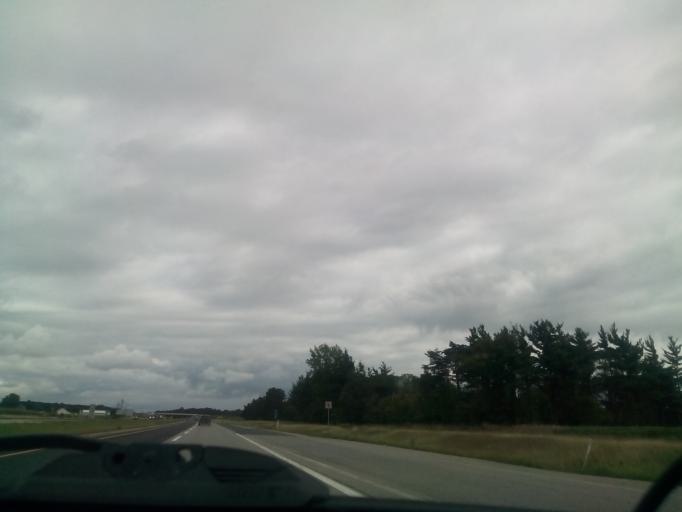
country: US
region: Michigan
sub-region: Saint Joseph County
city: Sturgis
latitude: 41.7452
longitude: -85.3266
